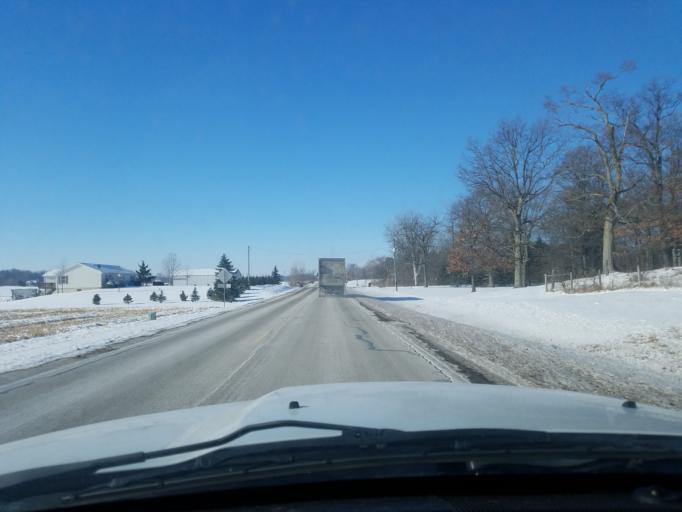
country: US
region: Indiana
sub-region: Noble County
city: Kendallville
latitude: 41.3954
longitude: -85.3310
